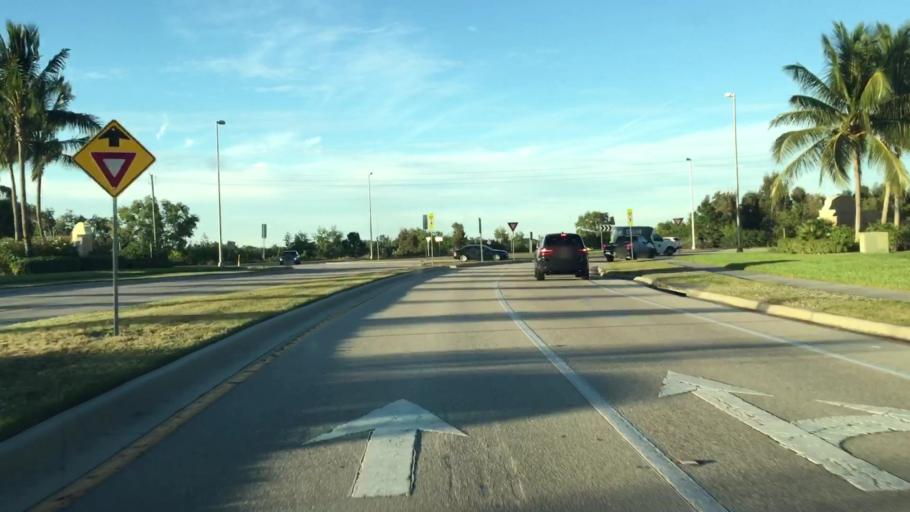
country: US
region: Florida
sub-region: Lee County
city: Estero
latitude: 26.4195
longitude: -81.8067
